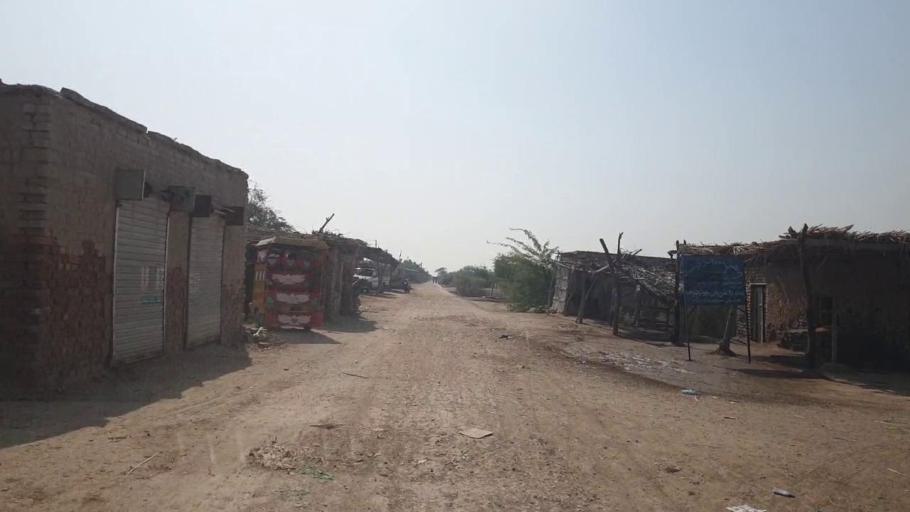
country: PK
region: Sindh
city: Berani
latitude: 25.8942
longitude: 68.7500
